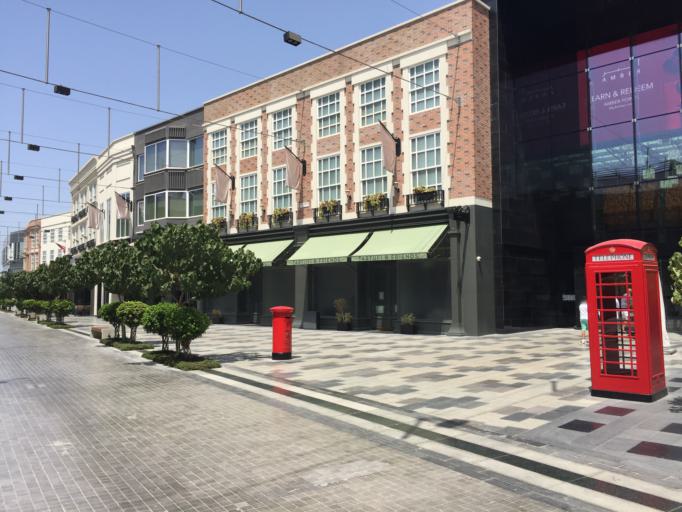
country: AE
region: Dubai
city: Dubai
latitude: 25.2078
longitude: 55.2622
